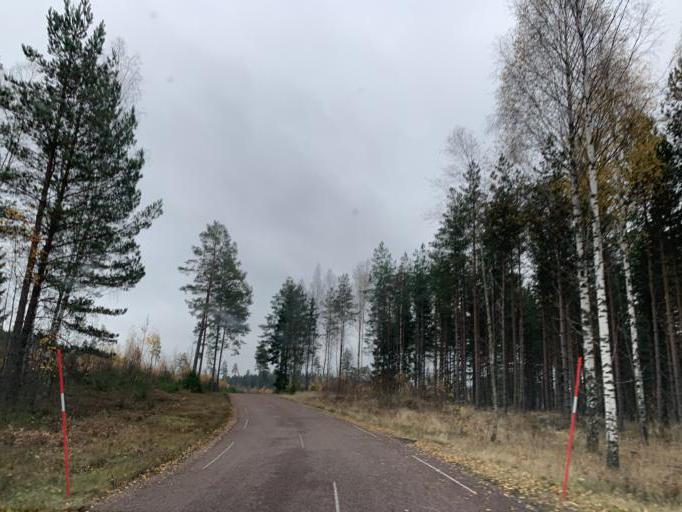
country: SE
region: Vaestmanland
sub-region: Surahammars Kommun
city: Surahammar
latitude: 59.6674
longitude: 16.0809
